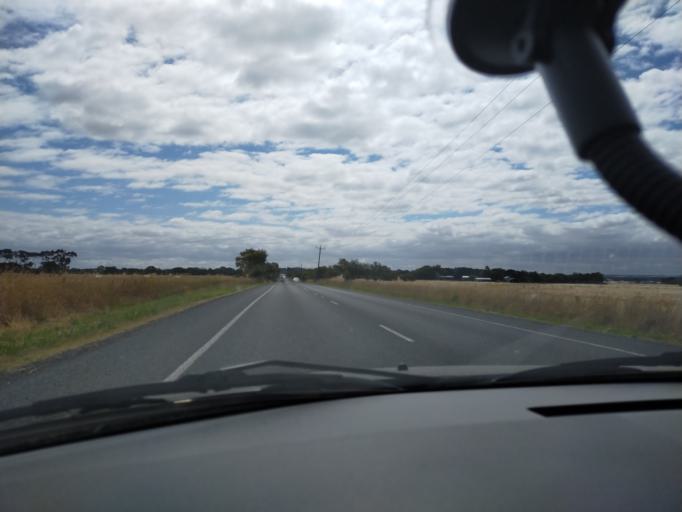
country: AU
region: Victoria
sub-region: Greater Geelong
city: Breakwater
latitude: -38.2537
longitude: 144.3770
